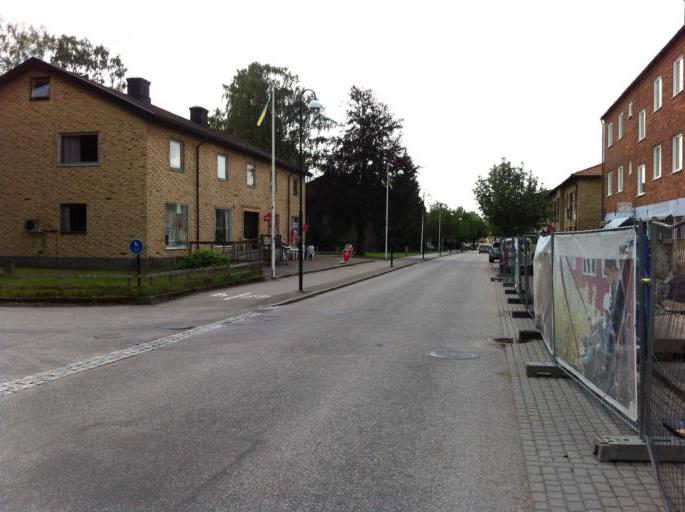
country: SE
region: Halland
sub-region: Hylte Kommun
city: Hyltebruk
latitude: 57.0009
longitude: 13.2415
